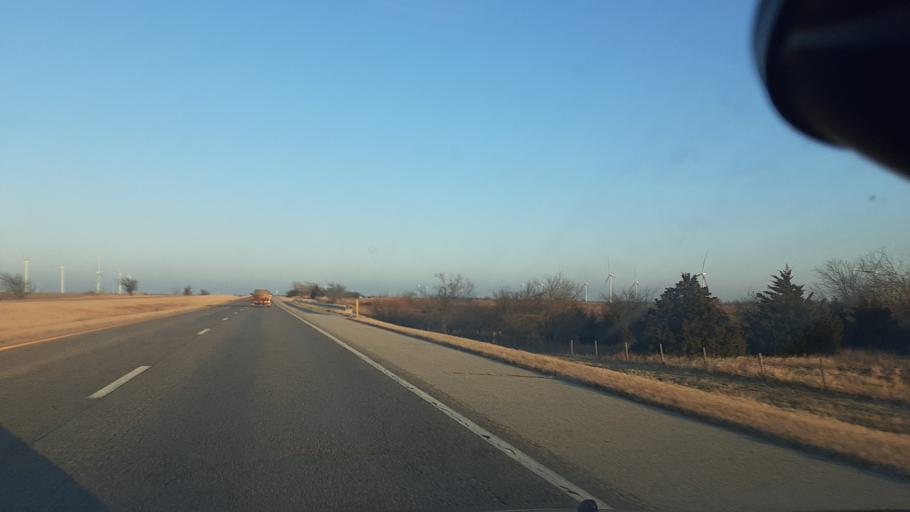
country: US
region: Oklahoma
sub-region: Noble County
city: Perry
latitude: 36.3975
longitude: -97.5232
